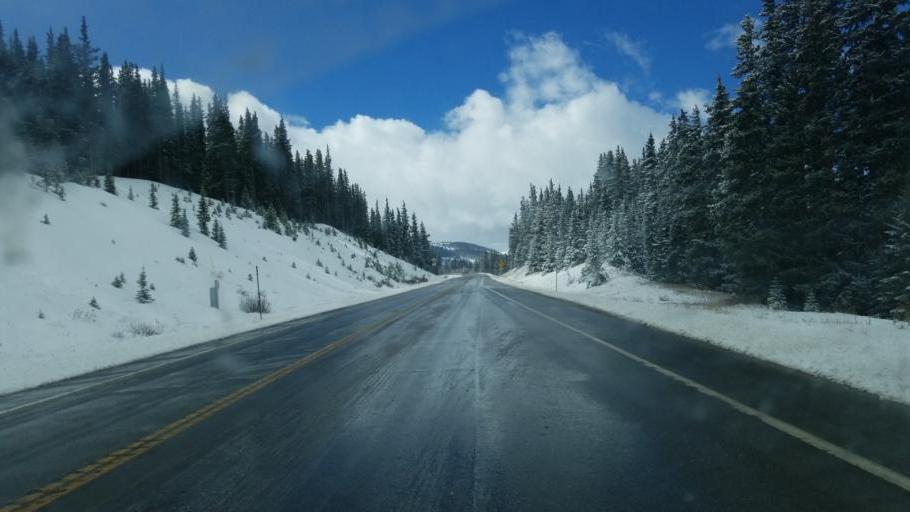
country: US
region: Colorado
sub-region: Summit County
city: Breckenridge
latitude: 39.4103
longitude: -106.1803
